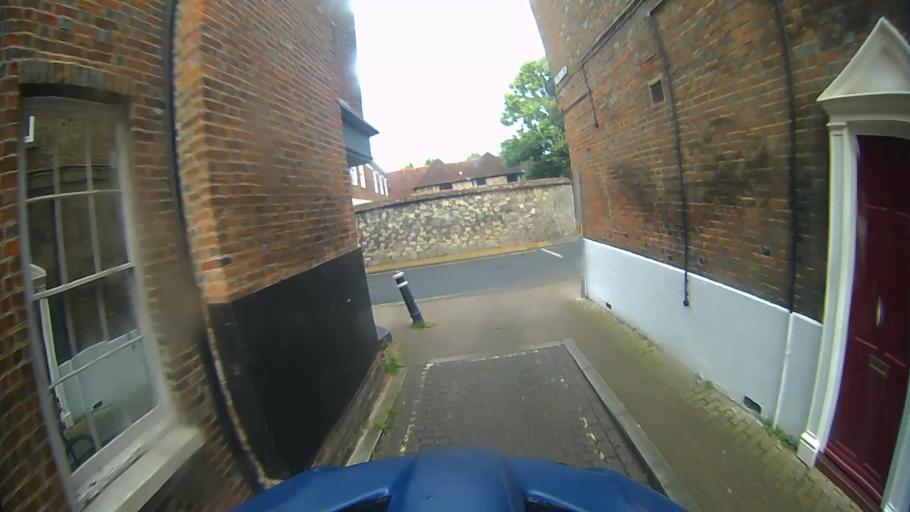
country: GB
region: England
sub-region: Hampshire
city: Winchester
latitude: 51.0678
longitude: -1.3153
